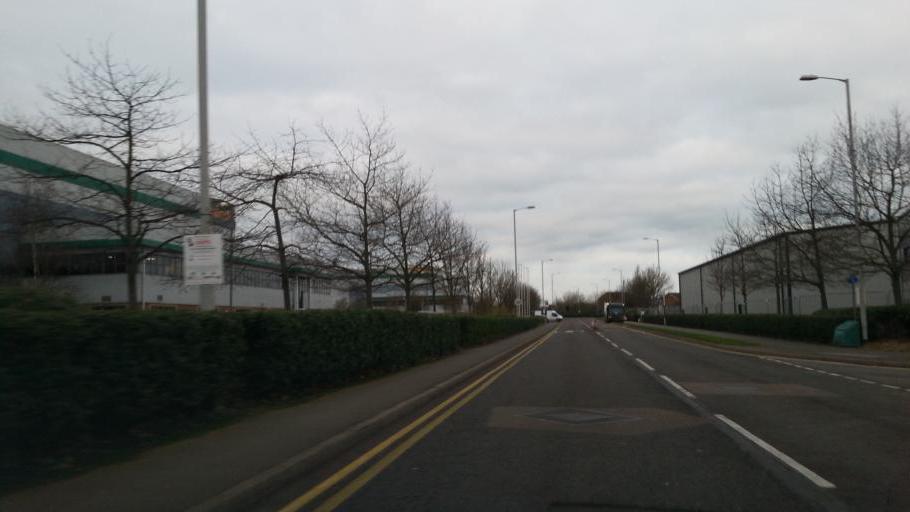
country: GB
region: England
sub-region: Coventry
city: Keresley
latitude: 52.4569
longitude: -1.5248
